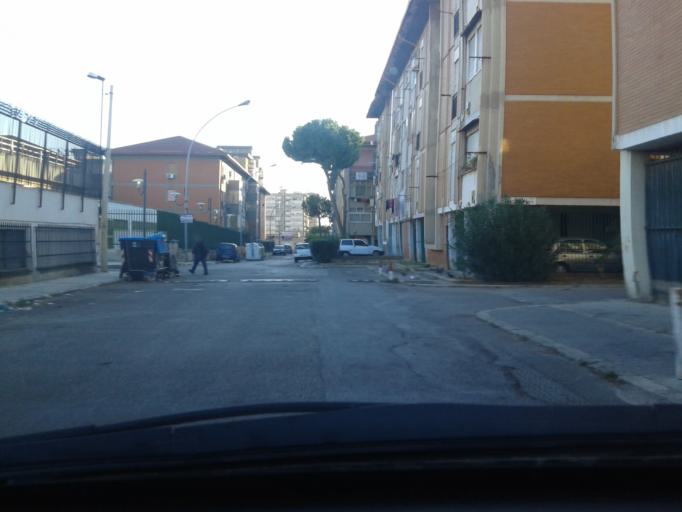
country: IT
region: Sicily
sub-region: Palermo
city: Ciaculli
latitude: 38.0899
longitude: 13.3607
